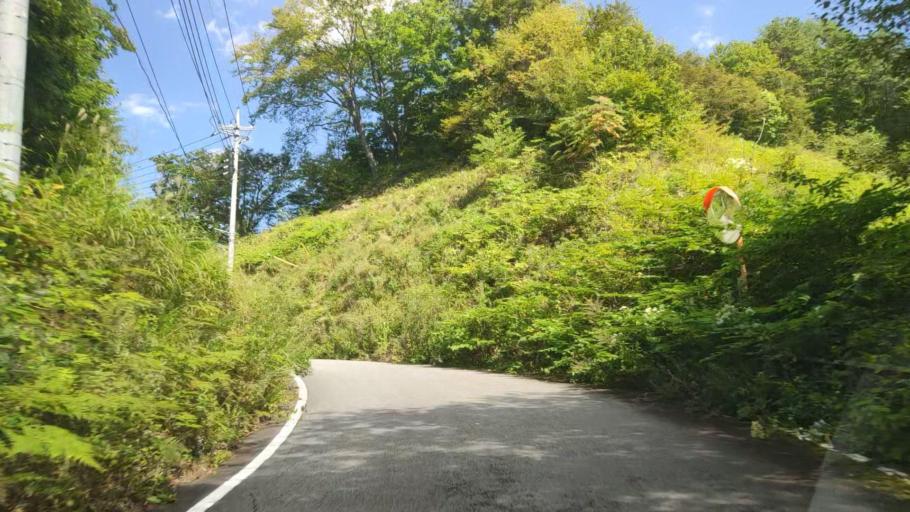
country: JP
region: Gunma
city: Nakanojomachi
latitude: 36.6391
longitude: 138.6110
